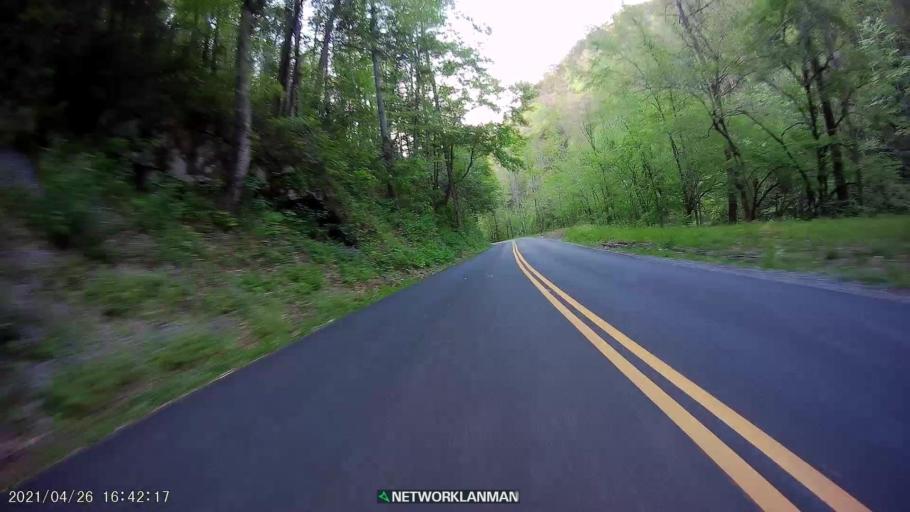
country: US
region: Tennessee
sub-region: Sevier County
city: Pigeon Forge
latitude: 35.6642
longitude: -83.6890
